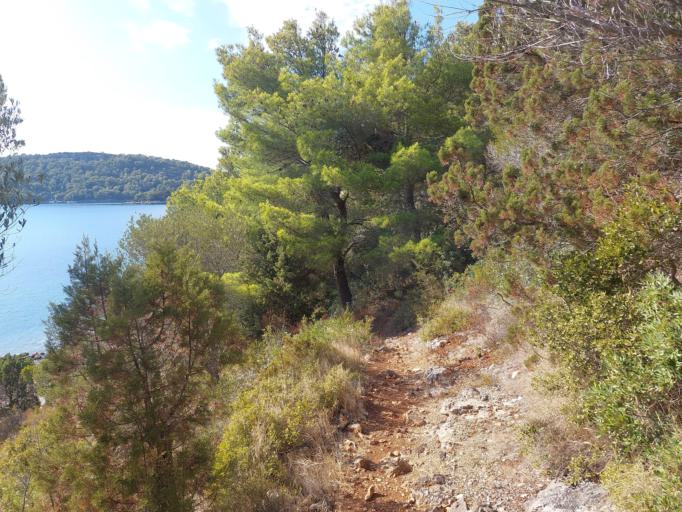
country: HR
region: Dubrovacko-Neretvanska
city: Smokvica
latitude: 42.7670
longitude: 16.8030
